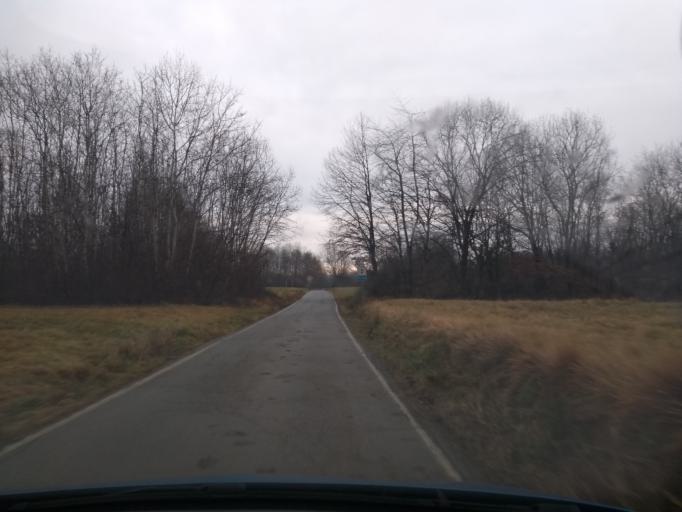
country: IT
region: Piedmont
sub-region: Provincia di Torino
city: Barbania
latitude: 45.2766
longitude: 7.6449
